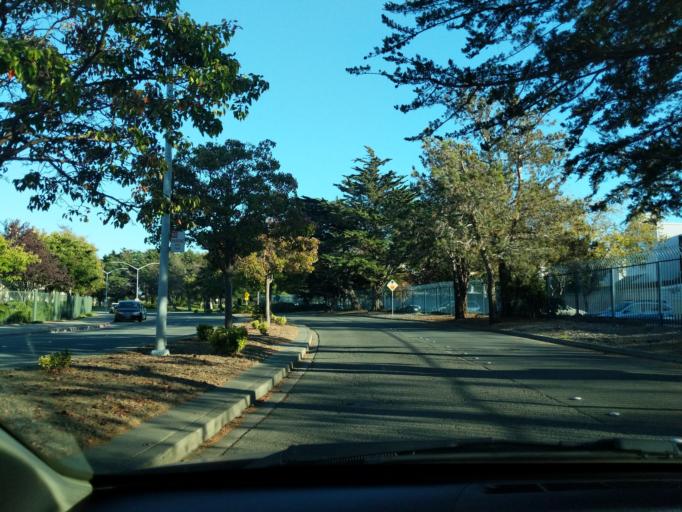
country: US
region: California
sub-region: Contra Costa County
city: Richmond
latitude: 37.9164
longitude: -122.3490
